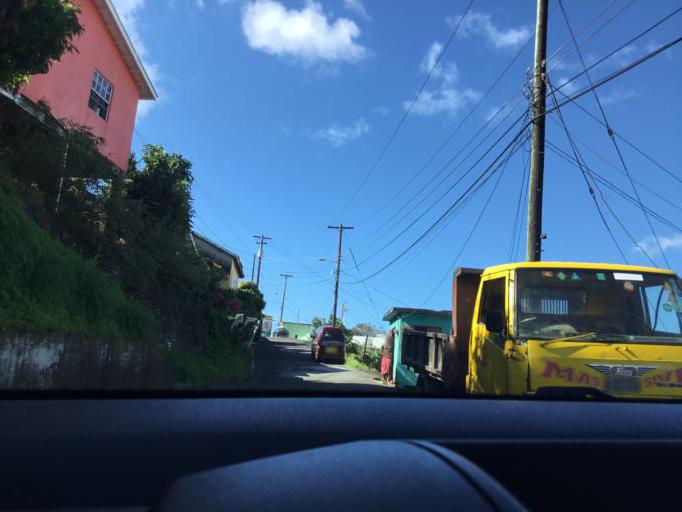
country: VC
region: Saint David
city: Chateaubelair
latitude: 13.2702
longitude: -61.2404
